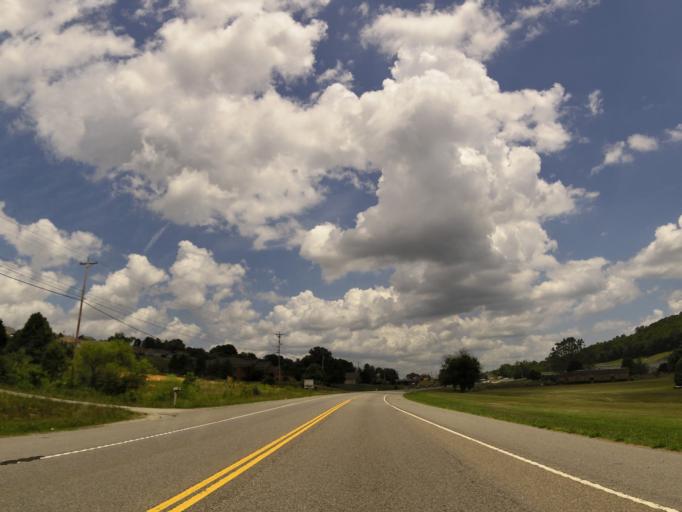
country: US
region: Tennessee
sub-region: Claiborne County
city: New Tazewell
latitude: 36.4240
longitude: -83.6363
